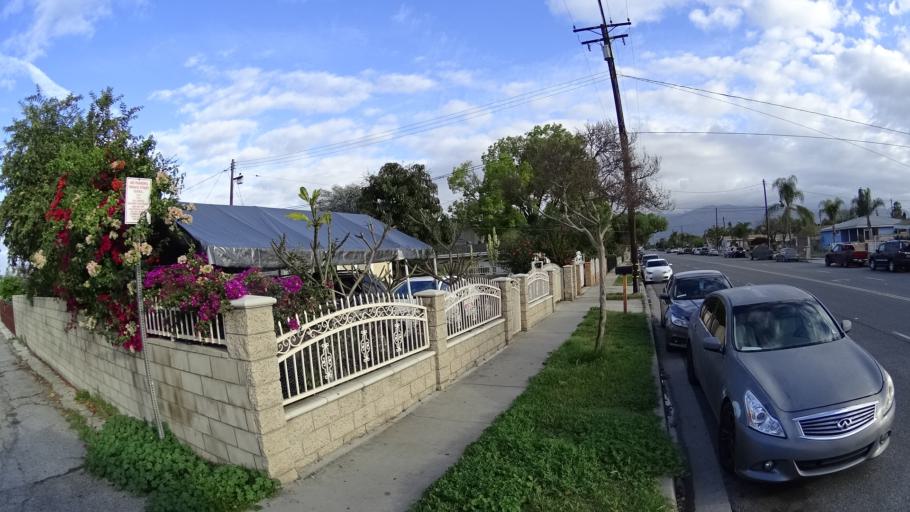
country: US
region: California
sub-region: Los Angeles County
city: Baldwin Park
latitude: 34.0933
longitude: -117.9737
